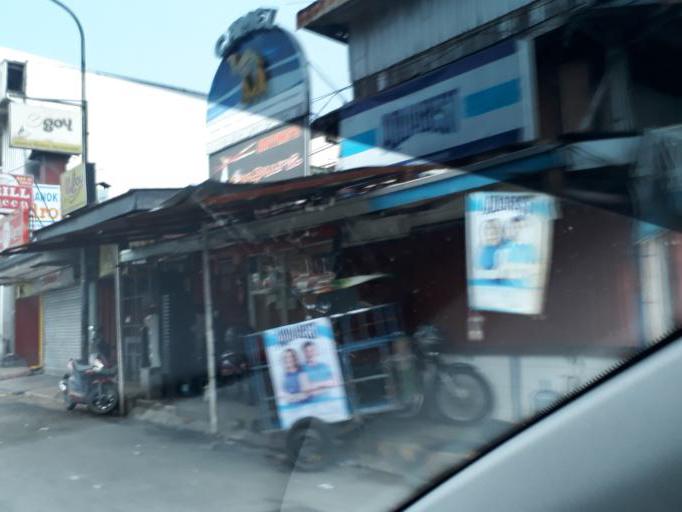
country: PH
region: Metro Manila
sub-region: City of Manila
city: Manila
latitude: 14.6270
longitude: 120.9926
